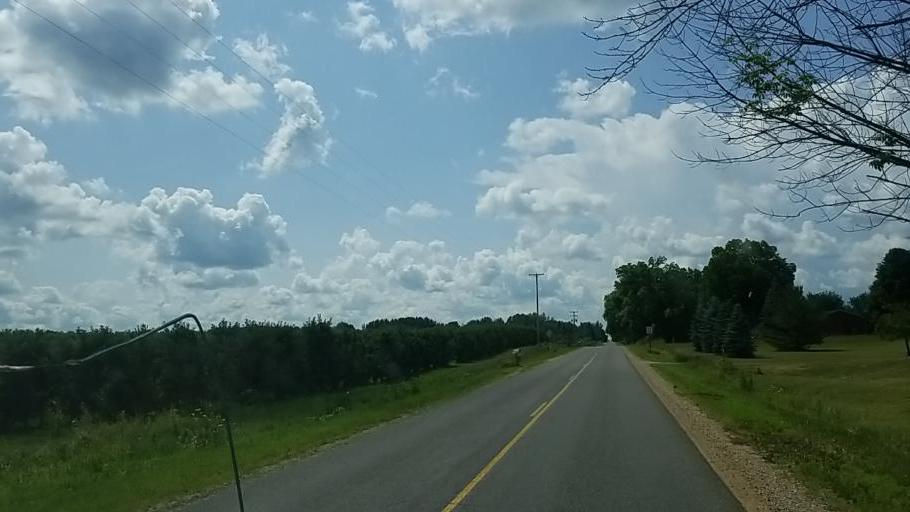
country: US
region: Michigan
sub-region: Muskegon County
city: Ravenna
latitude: 43.2339
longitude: -85.8797
